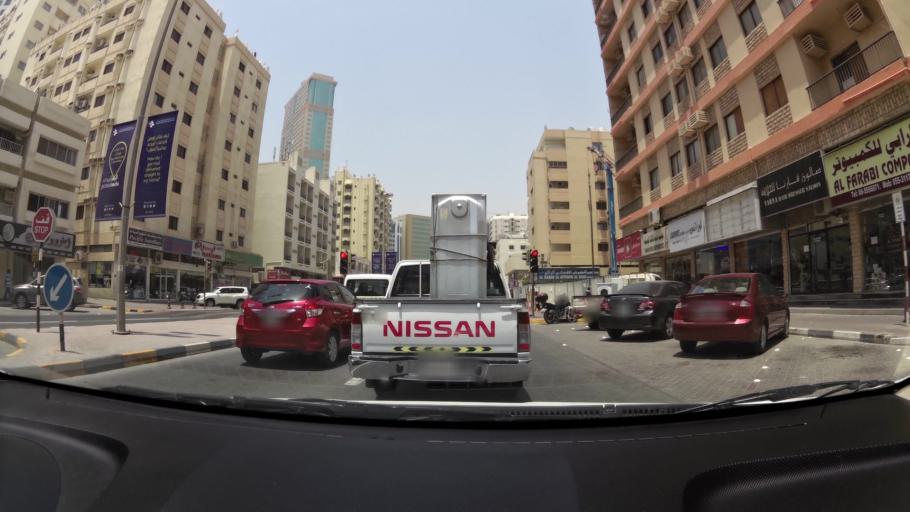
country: AE
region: Ash Shariqah
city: Sharjah
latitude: 25.3192
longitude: 55.3846
